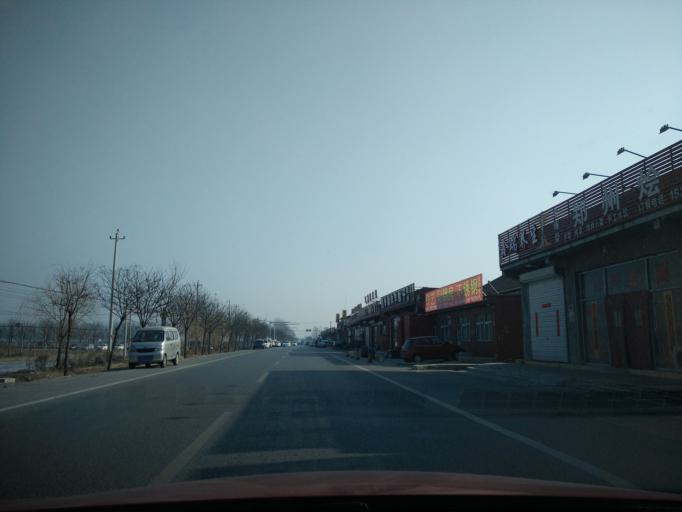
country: CN
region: Beijing
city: Yinghai
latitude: 39.7050
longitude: 116.4315
